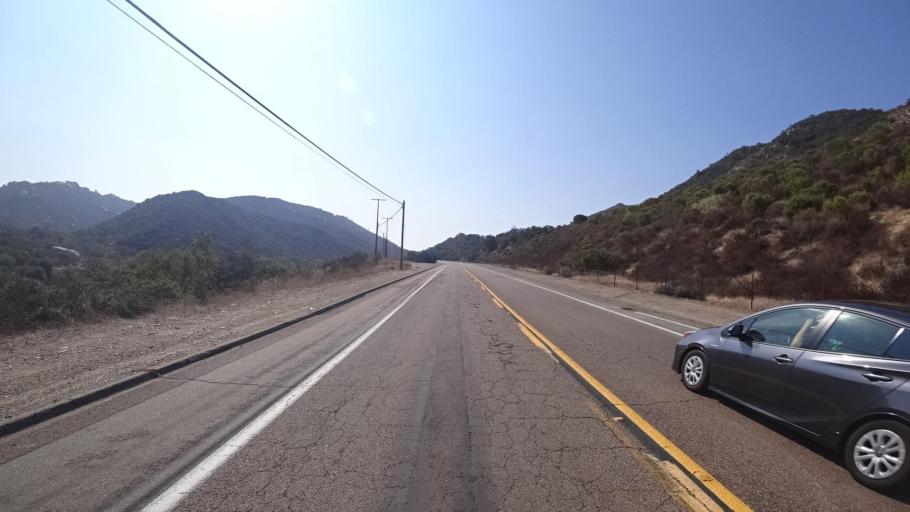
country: US
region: California
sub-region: San Diego County
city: Hidden Meadows
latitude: 33.2137
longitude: -117.1358
